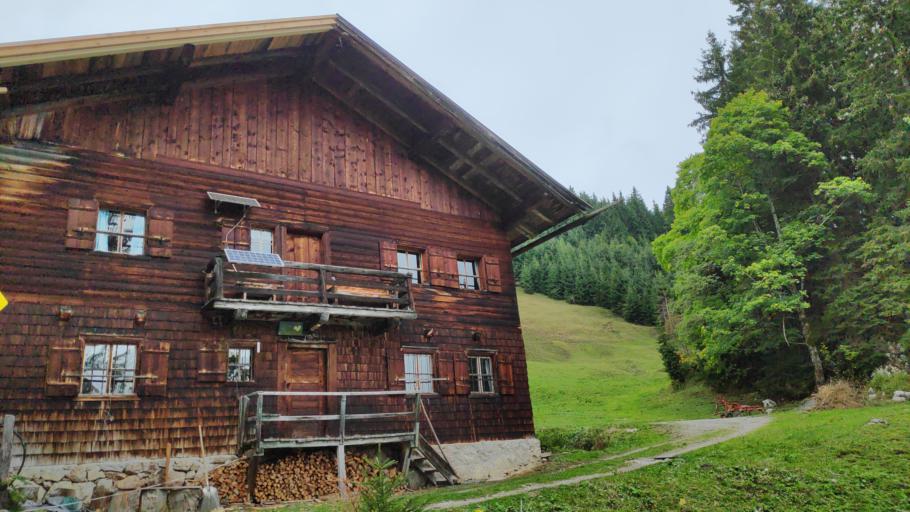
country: AT
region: Salzburg
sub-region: Politischer Bezirk Zell am See
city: Lofer
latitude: 47.6130
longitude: 12.6633
